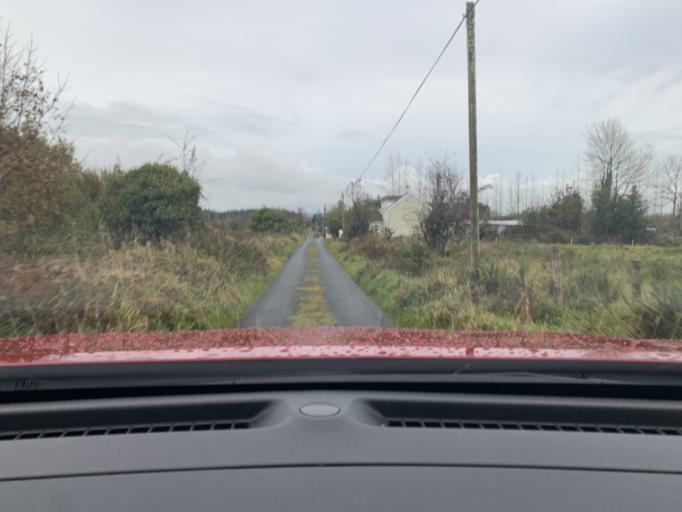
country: IE
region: Connaught
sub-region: Roscommon
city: Ballaghaderreen
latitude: 53.9229
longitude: -8.5618
